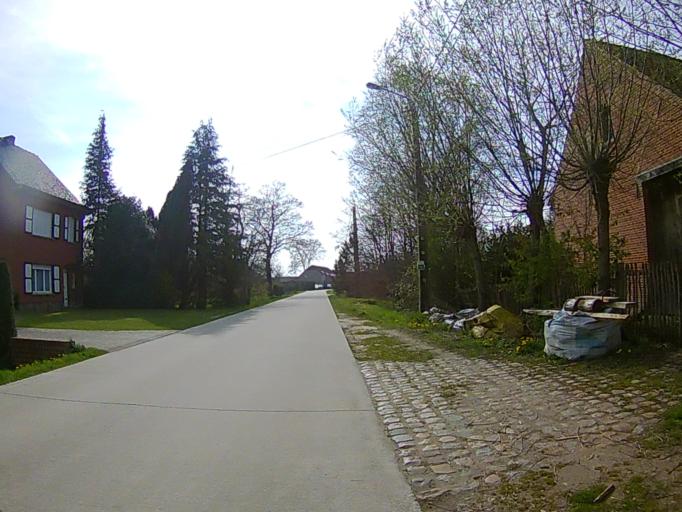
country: BE
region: Flanders
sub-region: Provincie Antwerpen
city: Kasterlee
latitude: 51.2157
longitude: 4.9245
